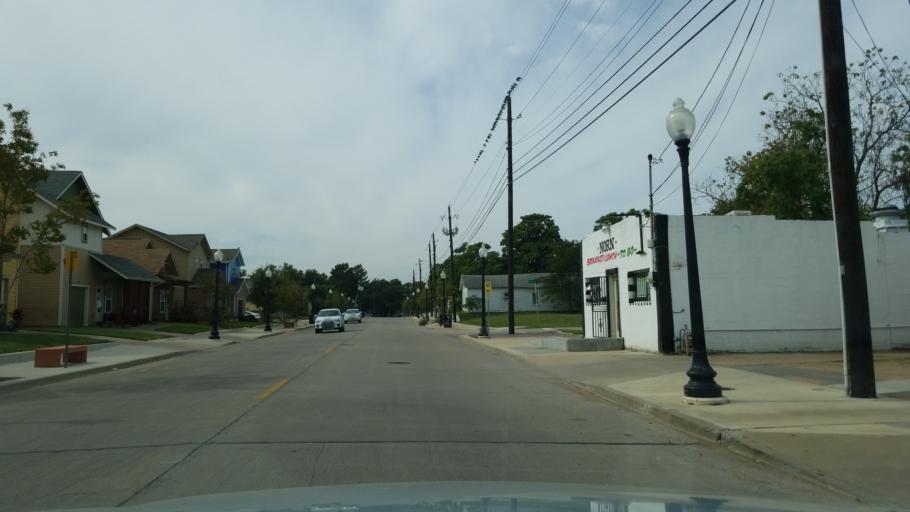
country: US
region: Texas
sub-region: Dallas County
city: Dallas
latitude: 32.7764
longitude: -96.7397
